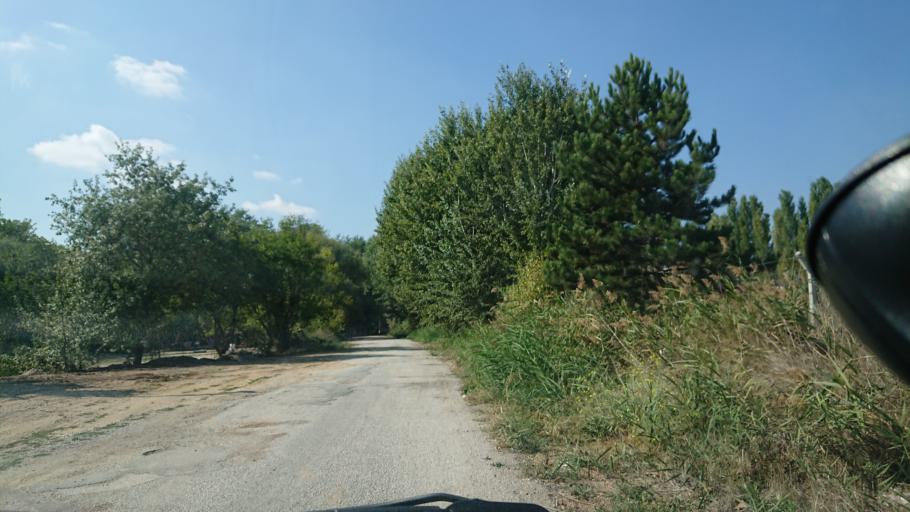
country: TR
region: Eskisehir
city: Eskisehir
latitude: 39.7544
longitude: 30.4752
